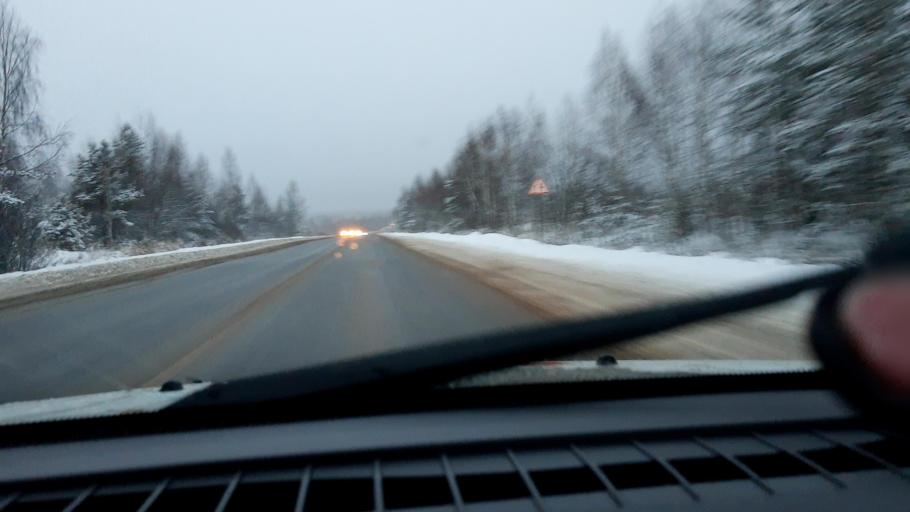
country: RU
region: Nizjnij Novgorod
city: Semenov
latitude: 56.8305
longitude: 44.6130
